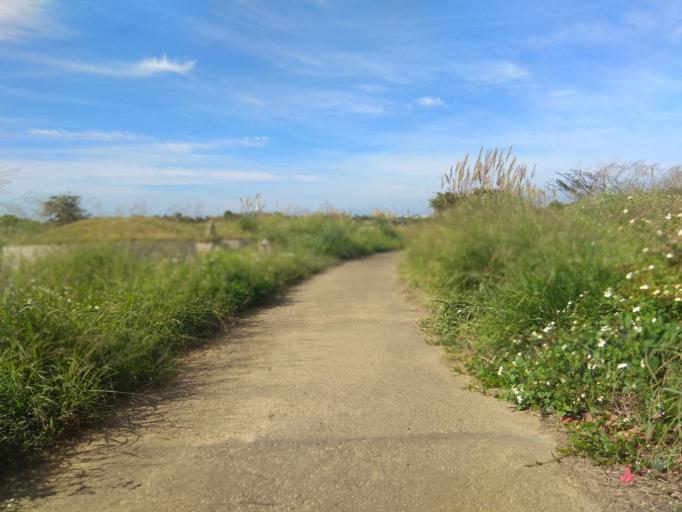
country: TW
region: Taiwan
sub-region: Hsinchu
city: Zhubei
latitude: 25.0195
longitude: 121.0687
